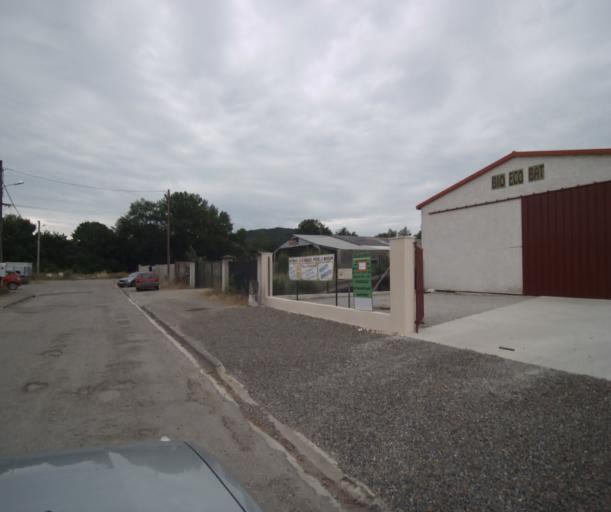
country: FR
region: Languedoc-Roussillon
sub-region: Departement de l'Aude
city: Limoux
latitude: 43.0784
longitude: 2.2264
